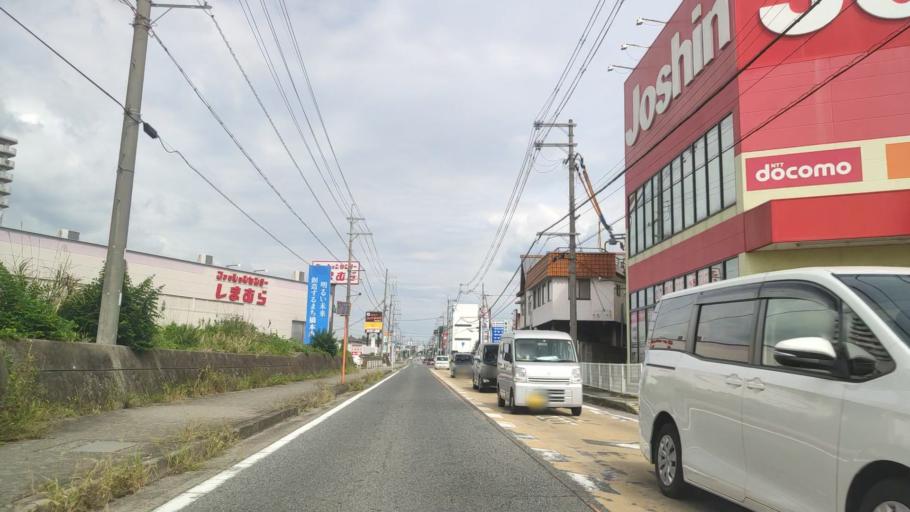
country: JP
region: Wakayama
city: Hashimoto
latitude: 34.3087
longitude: 135.5763
